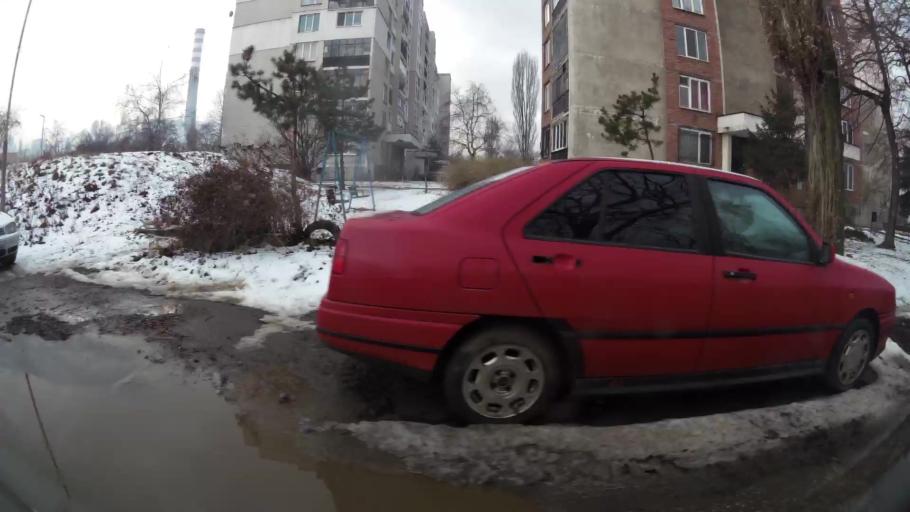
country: BG
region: Sofia-Capital
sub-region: Stolichna Obshtina
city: Sofia
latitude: 42.6912
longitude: 23.2863
